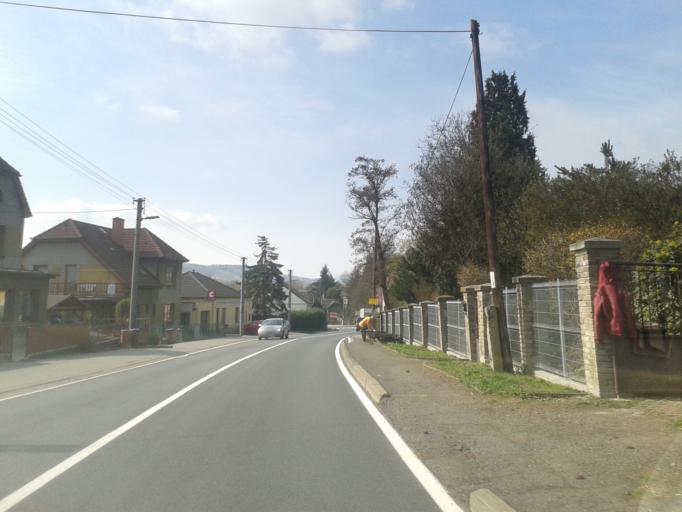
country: CZ
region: Central Bohemia
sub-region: Okres Beroun
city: Horovice
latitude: 49.8456
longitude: 13.9060
